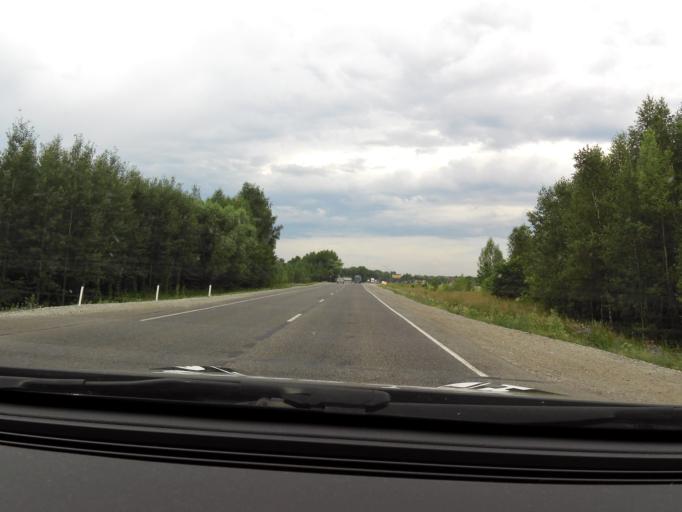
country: RU
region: Bashkortostan
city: Ulu-Telyak
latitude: 54.8332
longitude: 56.9897
